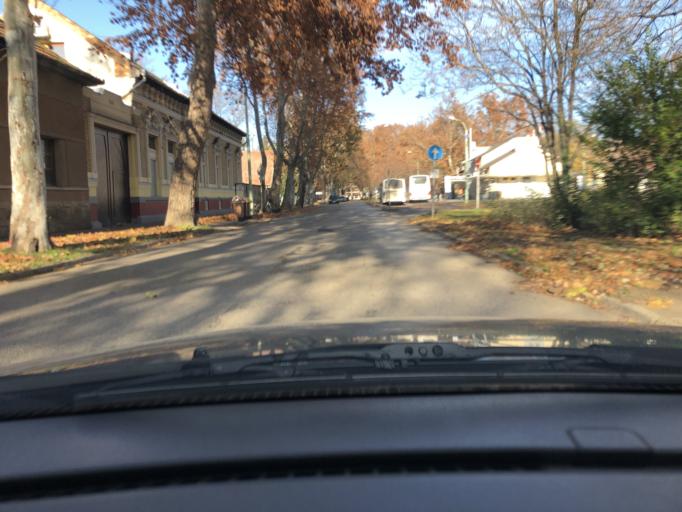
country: HU
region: Csongrad
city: Csongrad
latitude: 46.7078
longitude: 20.1476
